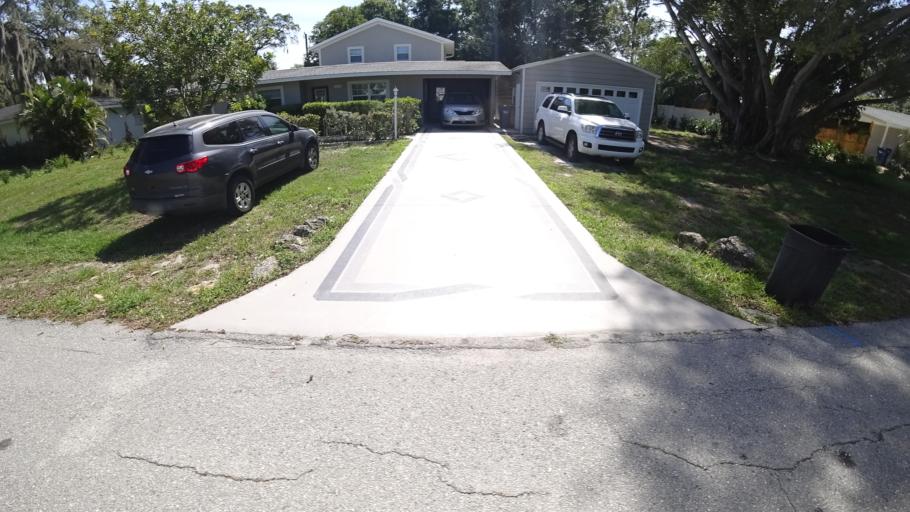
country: US
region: Florida
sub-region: Manatee County
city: West Bradenton
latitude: 27.5095
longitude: -82.6278
